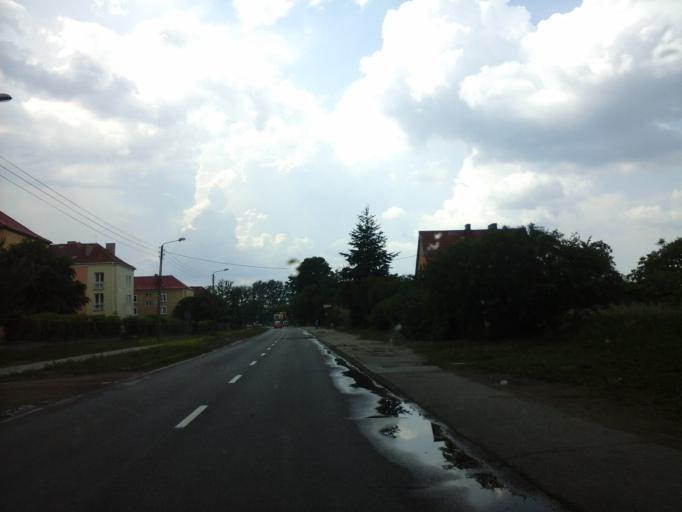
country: PL
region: West Pomeranian Voivodeship
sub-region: Powiat choszczenski
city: Choszczno
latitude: 53.1675
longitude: 15.4408
